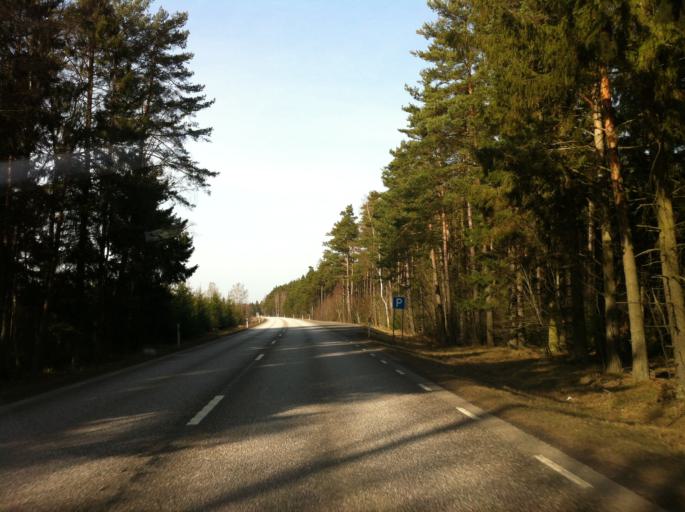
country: SE
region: Vaestra Goetaland
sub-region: Tidaholms Kommun
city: Tidaholm
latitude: 58.1992
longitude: 13.8888
